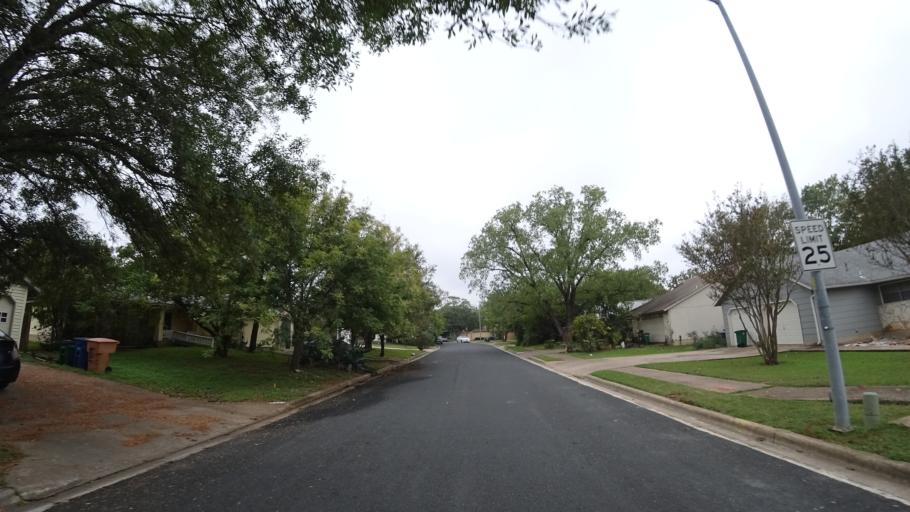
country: US
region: Texas
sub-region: Travis County
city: Shady Hollow
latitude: 30.2010
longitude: -97.8399
